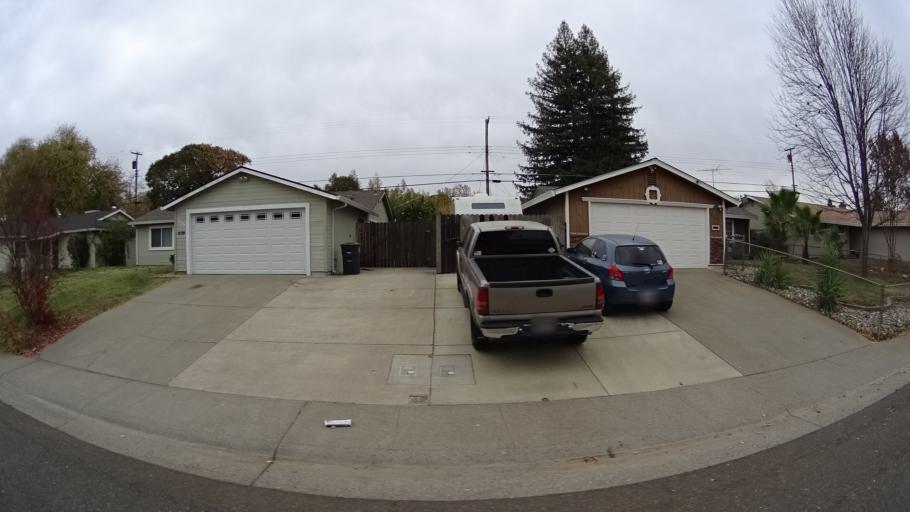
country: US
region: California
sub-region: Sacramento County
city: Citrus Heights
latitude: 38.6967
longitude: -121.3000
